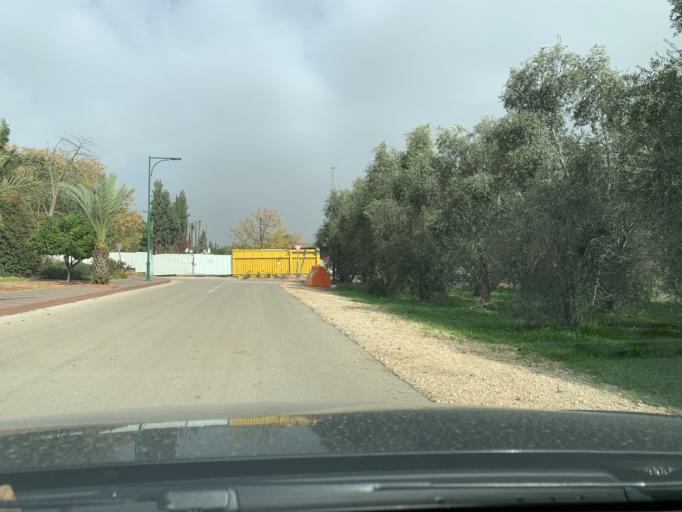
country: IL
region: Central District
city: Jaljulya
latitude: 32.1575
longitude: 34.9437
